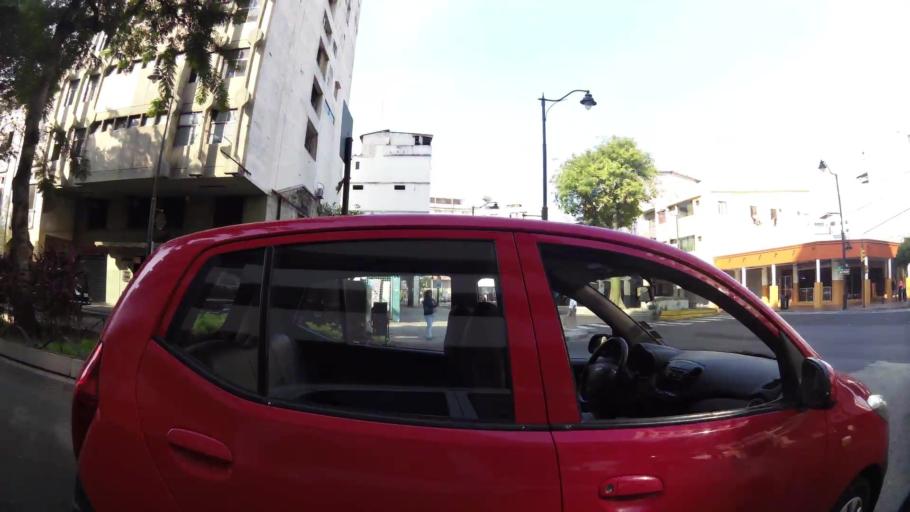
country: EC
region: Guayas
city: Guayaquil
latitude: -2.1964
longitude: -79.8851
